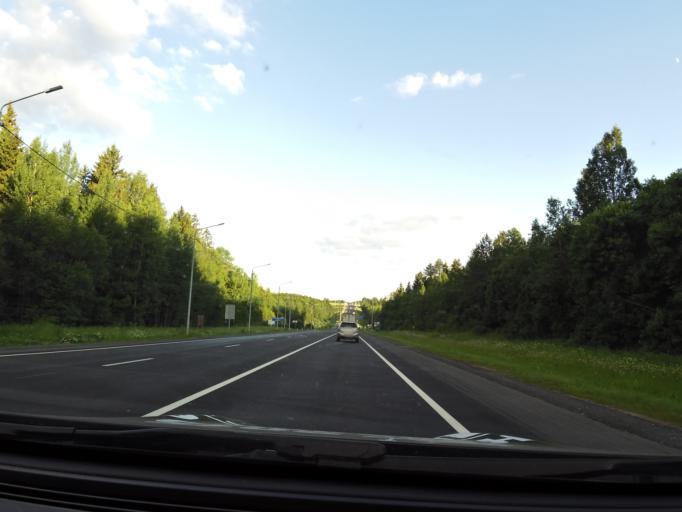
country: RU
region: Vologda
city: Gryazovets
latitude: 59.0303
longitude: 40.1112
